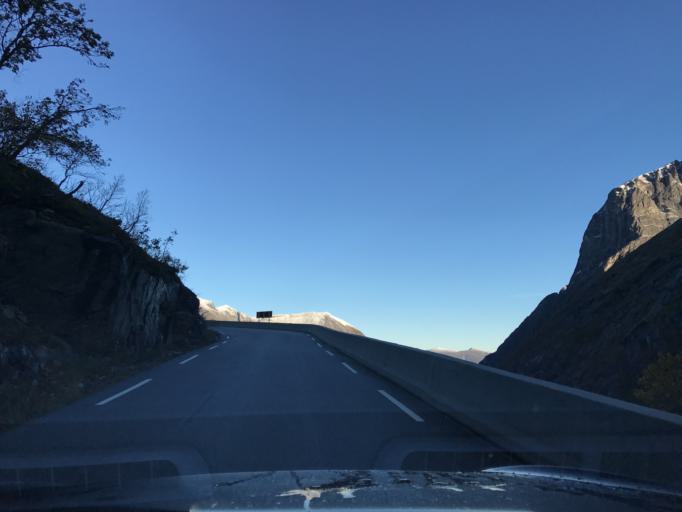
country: NO
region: More og Romsdal
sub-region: Rauma
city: Andalsnes
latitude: 62.4595
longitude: 7.6708
